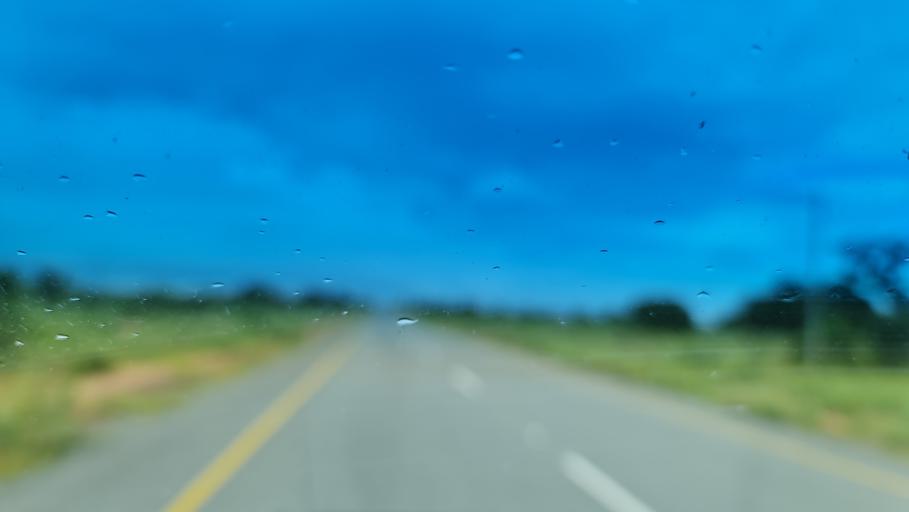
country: MZ
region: Nampula
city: Nampula
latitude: -15.5595
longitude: 39.3224
